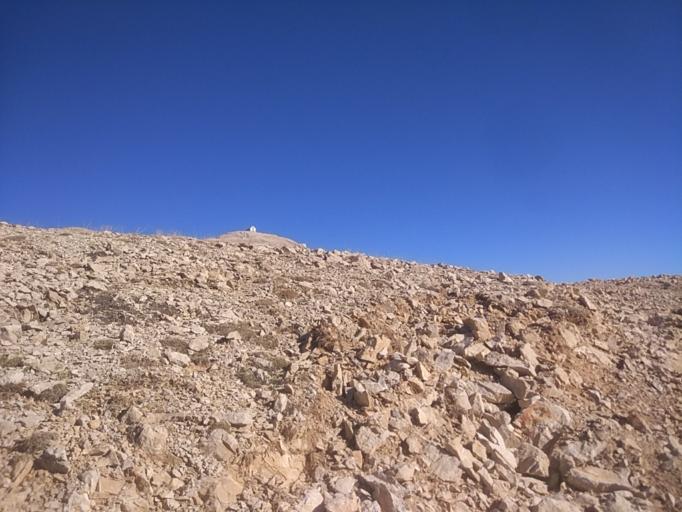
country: TR
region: Antalya
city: Altinyaka
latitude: 36.5397
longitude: 30.4265
